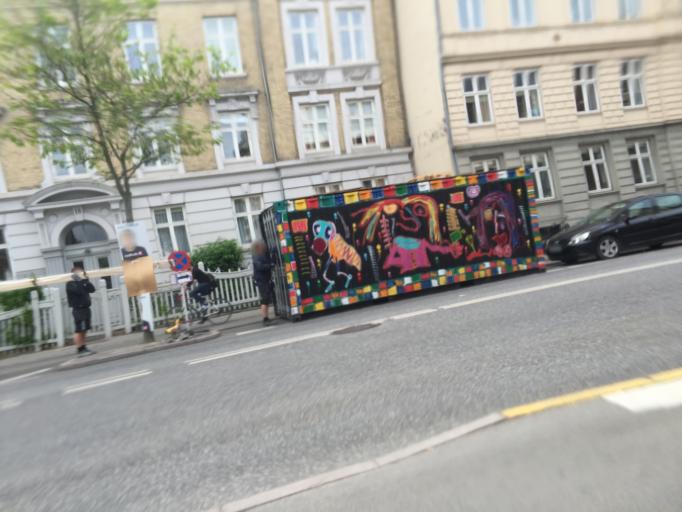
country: DK
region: Capital Region
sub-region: Frederiksberg Kommune
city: Frederiksberg
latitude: 55.6775
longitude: 12.5465
